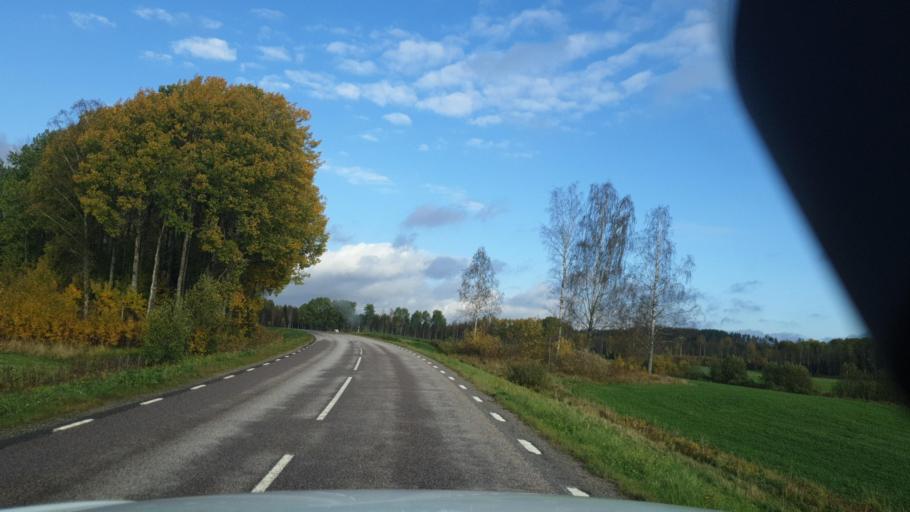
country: SE
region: Vaermland
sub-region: Arvika Kommun
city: Arvika
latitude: 59.4974
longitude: 12.6855
